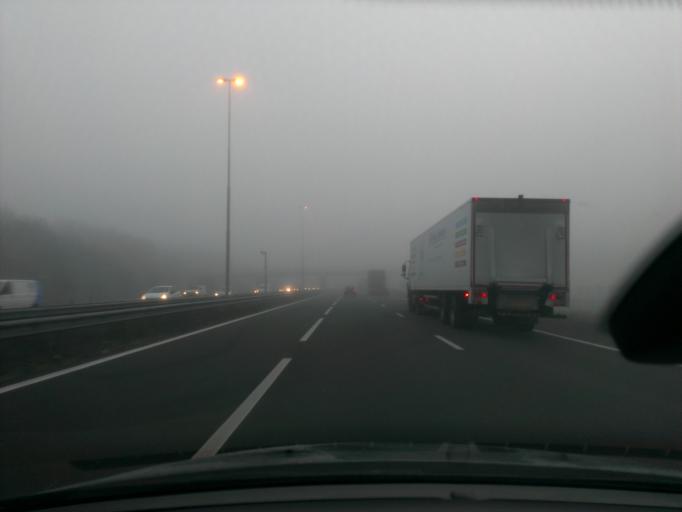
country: NL
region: Gelderland
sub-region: Gemeente Voorst
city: Twello
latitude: 52.2061
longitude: 6.0828
